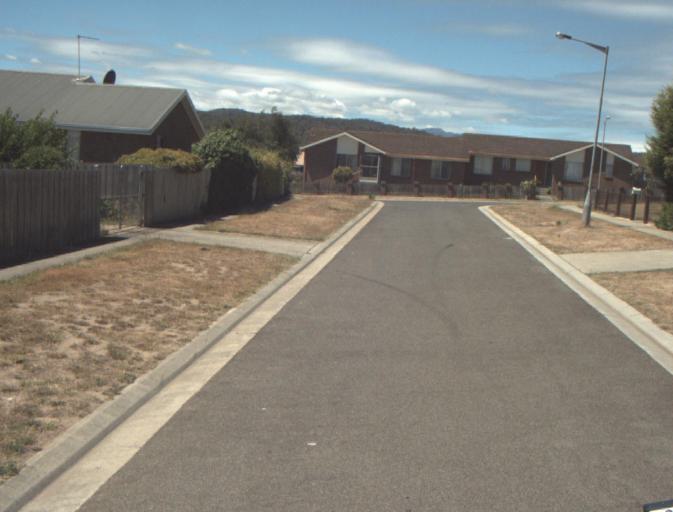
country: AU
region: Tasmania
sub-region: Launceston
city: Mayfield
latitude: -41.3748
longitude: 147.1396
